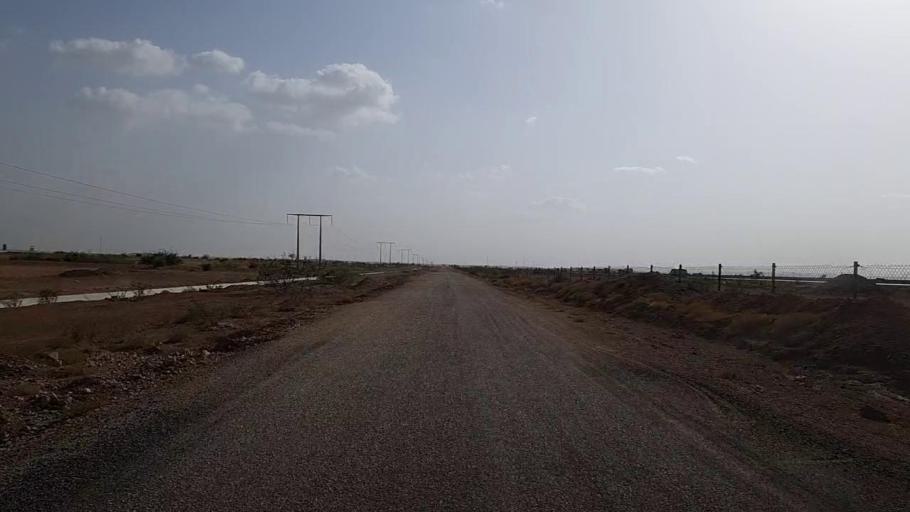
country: PK
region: Sindh
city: Kotri
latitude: 25.2692
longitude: 68.0025
